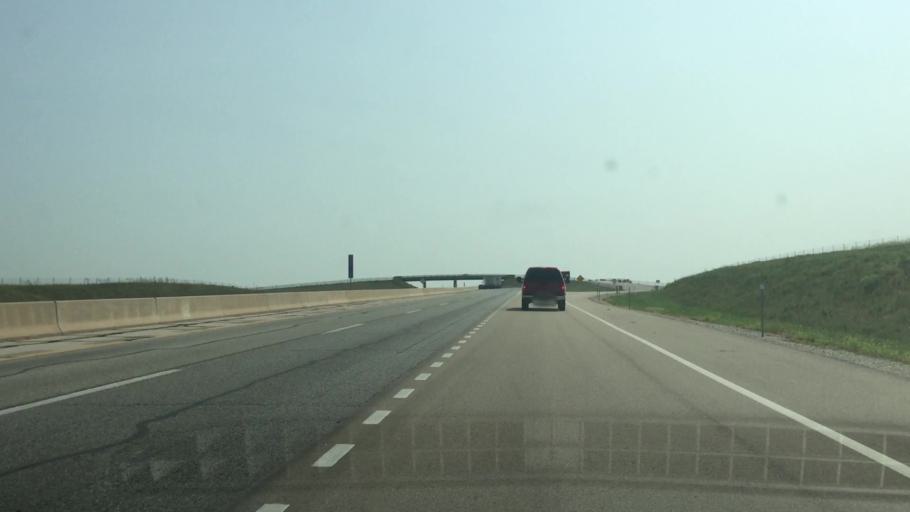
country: US
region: Kansas
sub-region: Chase County
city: Cottonwood Falls
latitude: 38.2284
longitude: -96.4137
